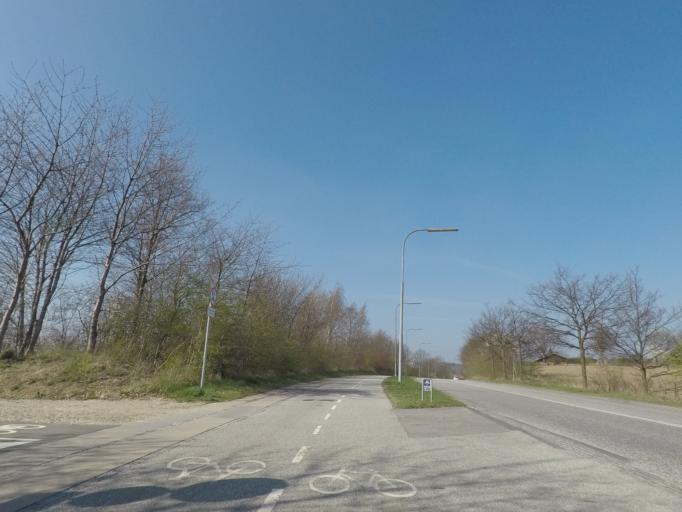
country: DK
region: Capital Region
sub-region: Ballerup Kommune
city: Ballerup
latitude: 55.7455
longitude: 12.3846
